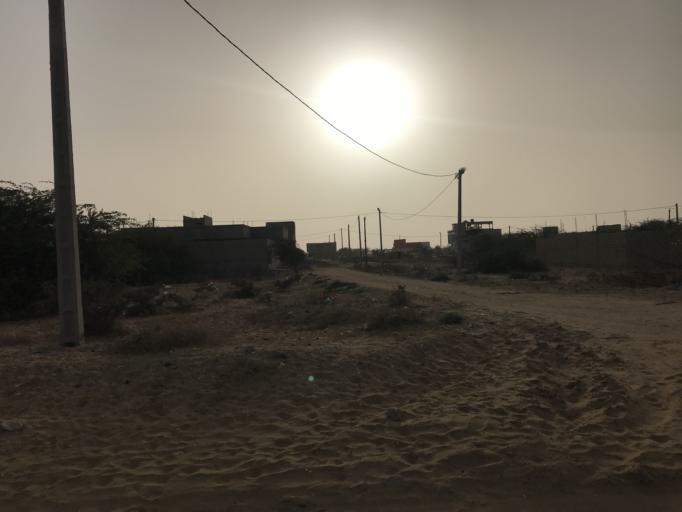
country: SN
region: Saint-Louis
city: Saint-Louis
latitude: 16.0306
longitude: -16.4449
